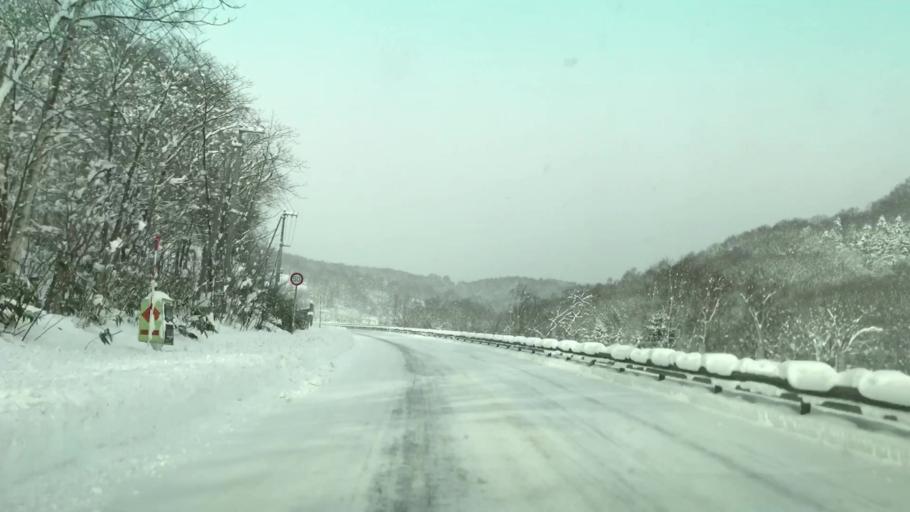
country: JP
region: Hokkaido
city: Yoichi
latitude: 43.2144
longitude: 140.7471
